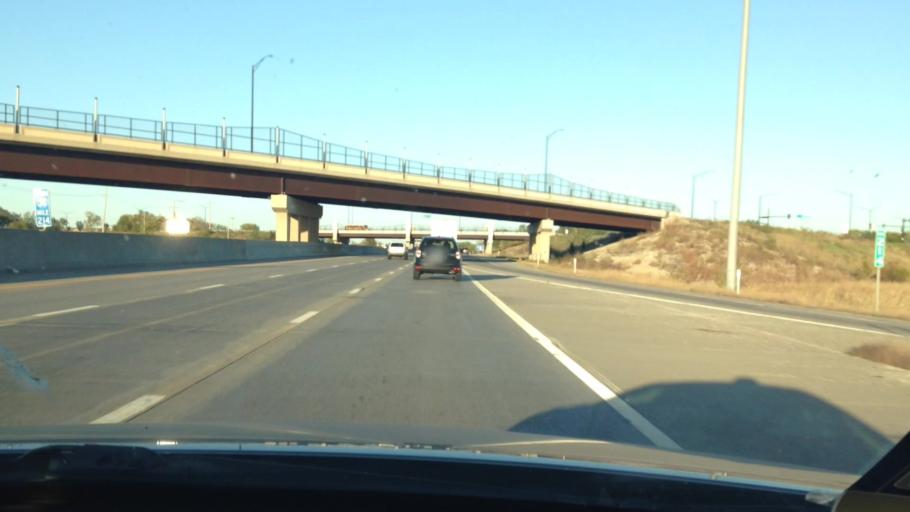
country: US
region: Kansas
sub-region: Johnson County
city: Olathe
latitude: 38.8393
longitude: -94.8376
